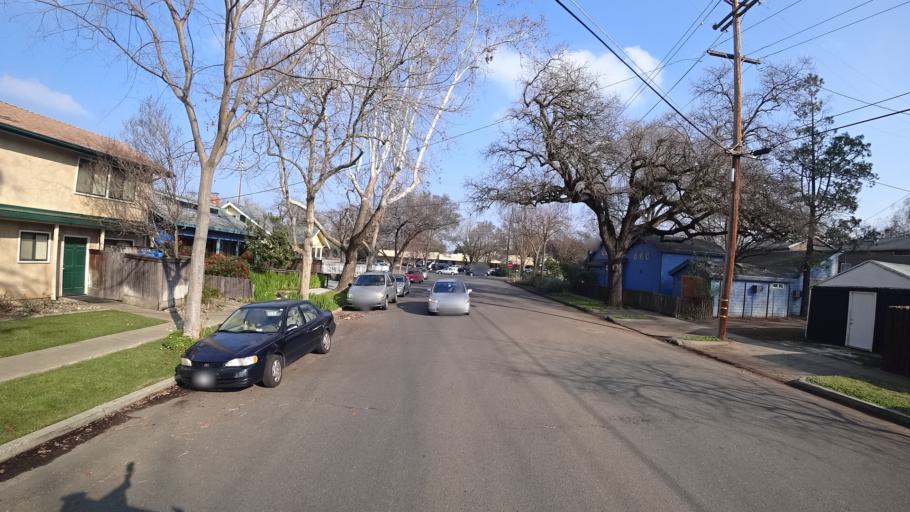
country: US
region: California
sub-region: Yolo County
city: Davis
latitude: 38.5502
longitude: -121.7415
